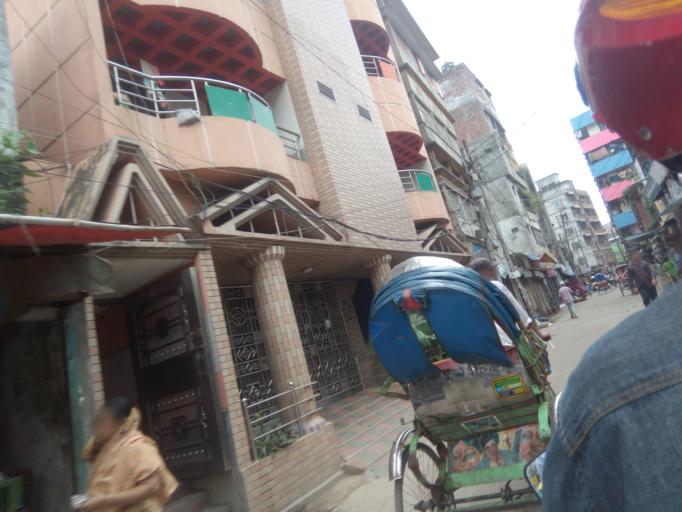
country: BD
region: Dhaka
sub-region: Dhaka
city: Dhaka
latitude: 23.7045
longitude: 90.4182
